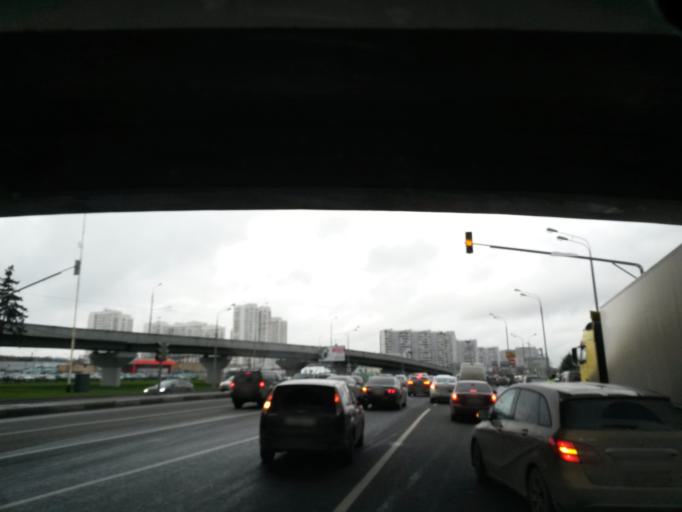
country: RU
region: Moscow
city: Annino
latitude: 55.5784
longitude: 37.5965
